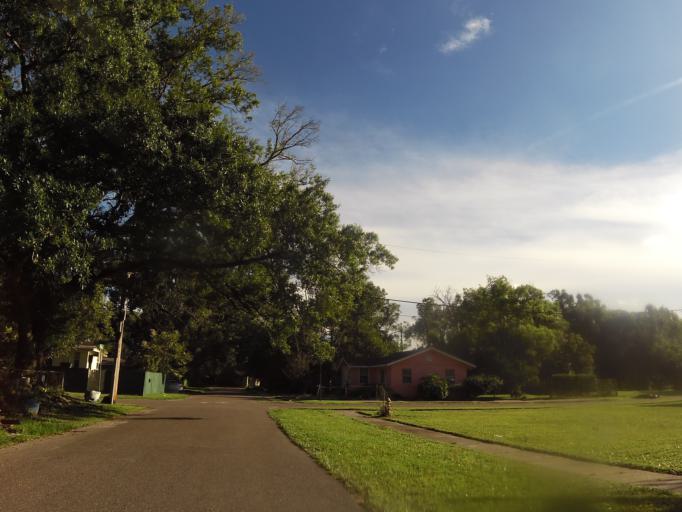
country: US
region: Florida
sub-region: Duval County
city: Jacksonville
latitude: 30.3488
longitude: -81.6898
